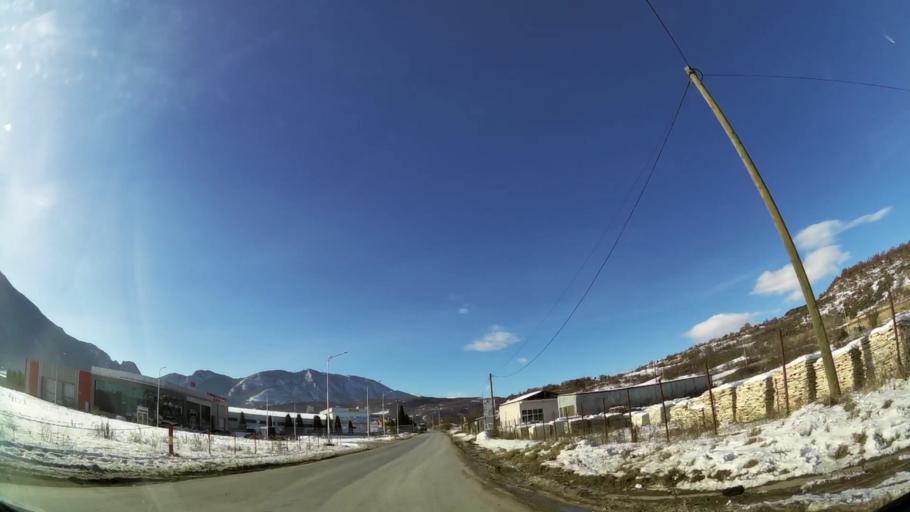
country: MK
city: Ljubin
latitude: 41.9902
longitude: 21.3130
